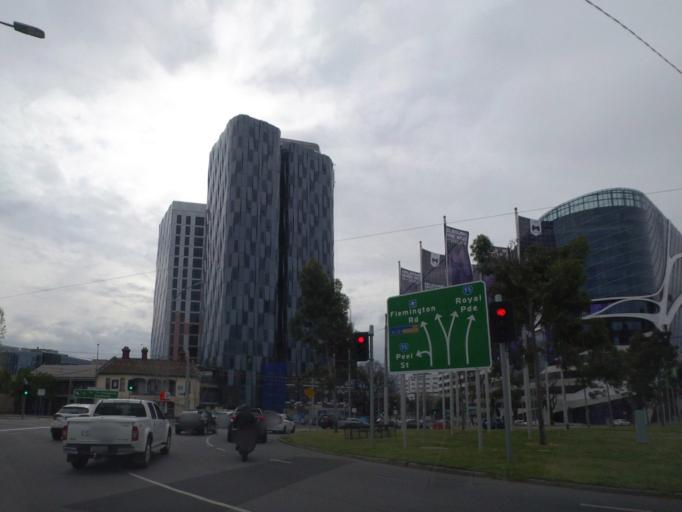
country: AU
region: Victoria
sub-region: Melbourne
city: North Melbourne
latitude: -37.8019
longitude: 144.9573
